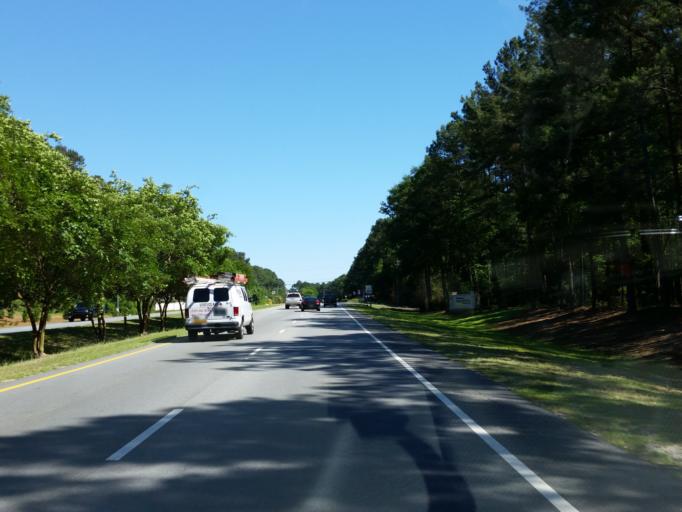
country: US
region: Georgia
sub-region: Lowndes County
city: Remerton
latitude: 30.8868
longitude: -83.3144
